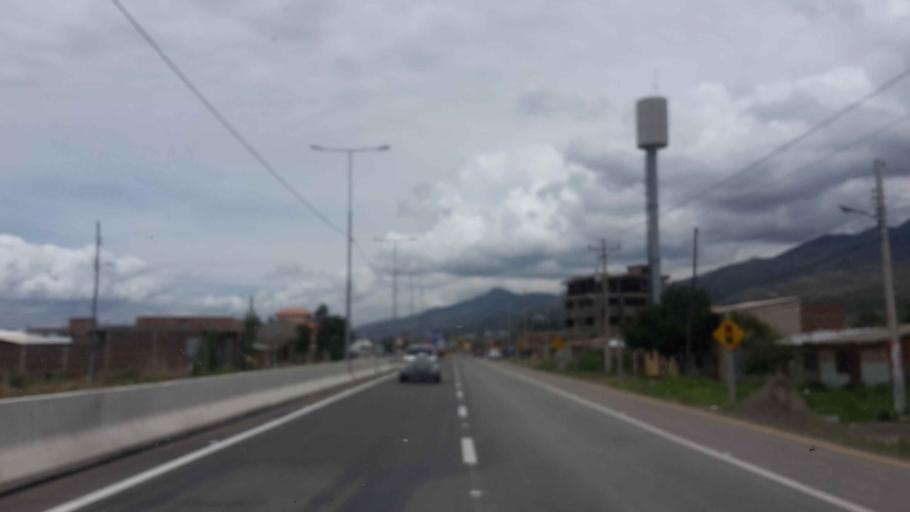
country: BO
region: Cochabamba
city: Punata
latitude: -17.5142
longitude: -65.8540
